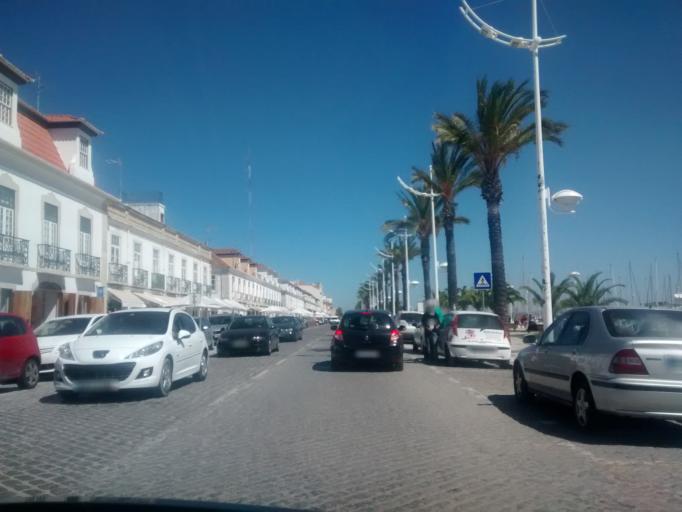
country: PT
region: Faro
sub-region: Vila Real de Santo Antonio
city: Vila Real de Santo Antonio
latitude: 37.1929
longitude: -7.4138
